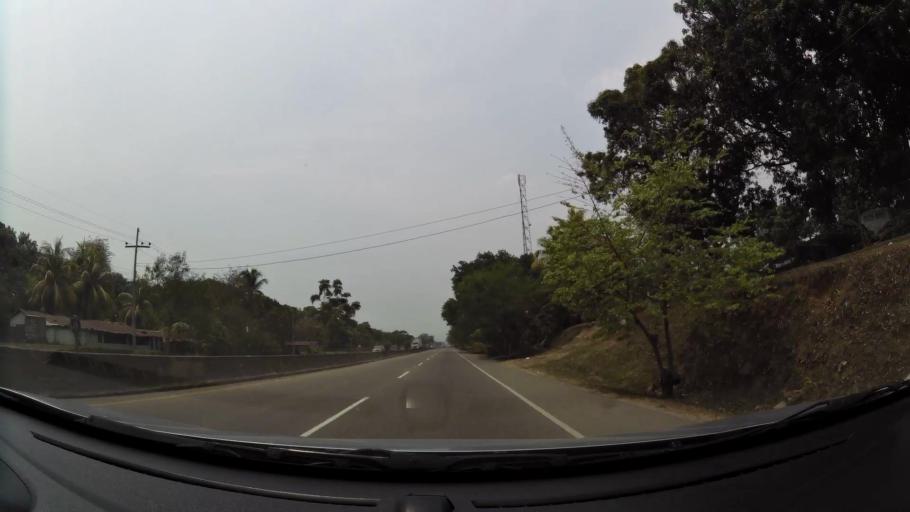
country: HN
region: Cortes
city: Oropendolas
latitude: 15.0383
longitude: -87.9281
